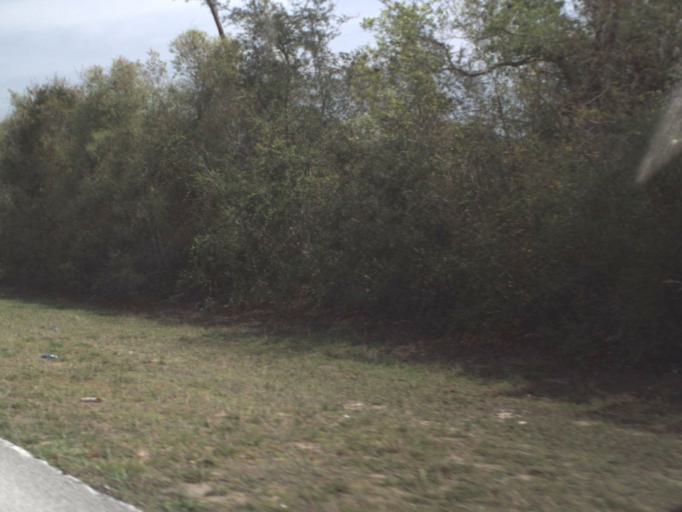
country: US
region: Florida
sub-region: Lake County
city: Astor
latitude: 29.1864
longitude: -81.6543
